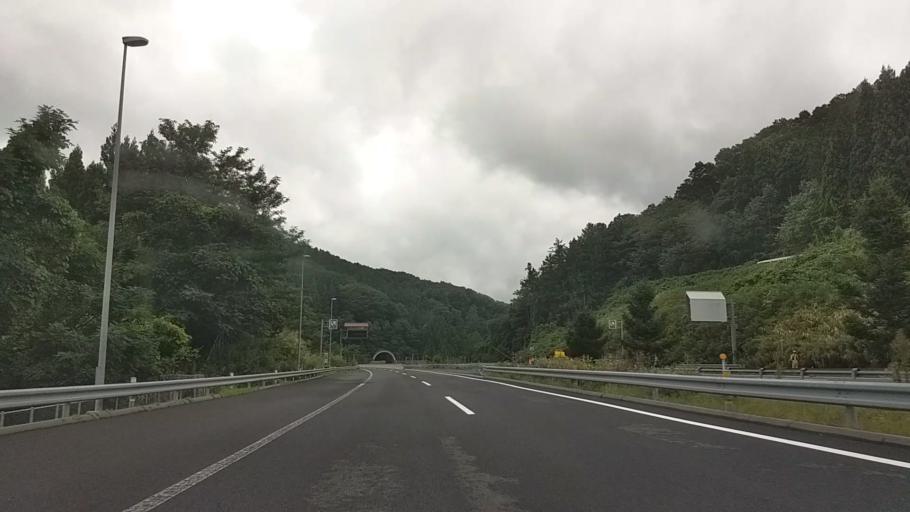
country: JP
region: Nagano
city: Iiyama
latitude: 36.8028
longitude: 138.3124
